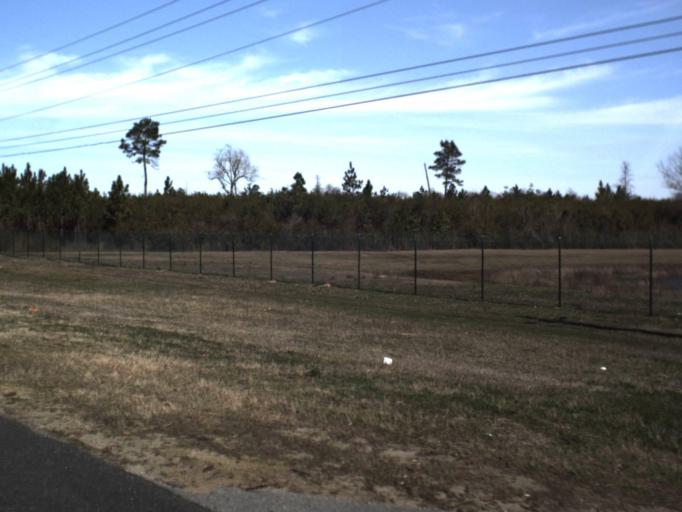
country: US
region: Florida
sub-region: Bay County
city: Lynn Haven
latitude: 30.3019
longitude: -85.6478
